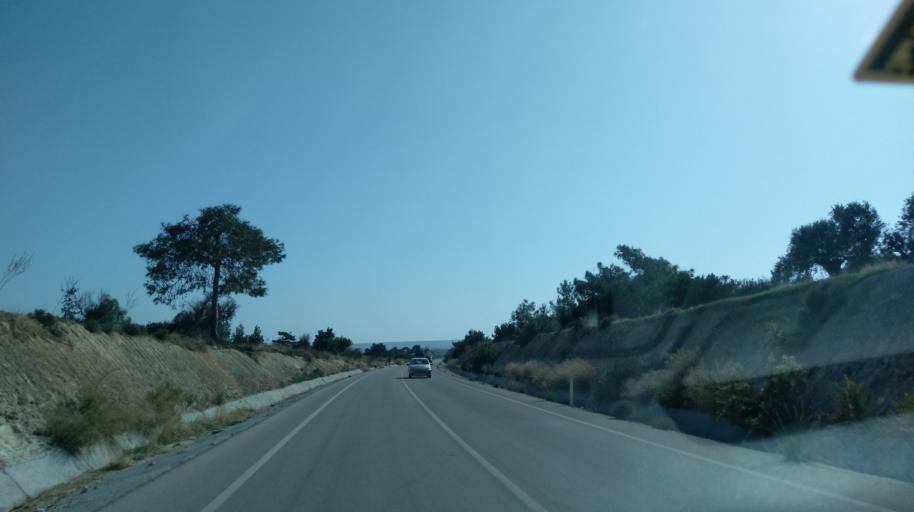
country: CY
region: Ammochostos
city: Trikomo
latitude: 35.4149
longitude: 33.9860
